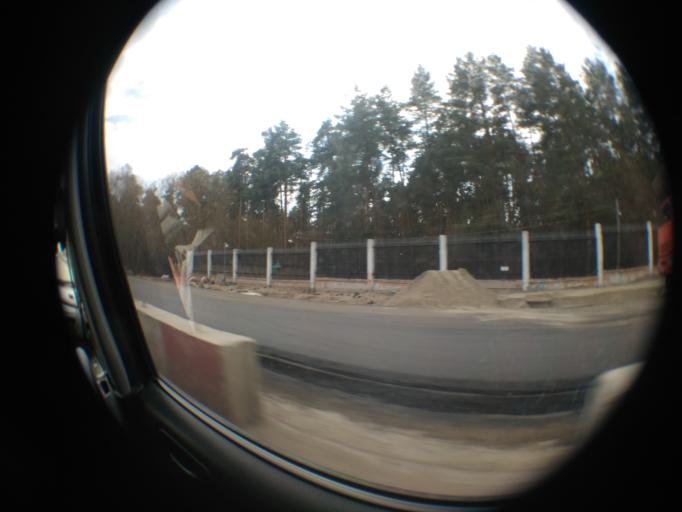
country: RU
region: Moskovskaya
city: Zhukovskiy
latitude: 55.5881
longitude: 38.1194
